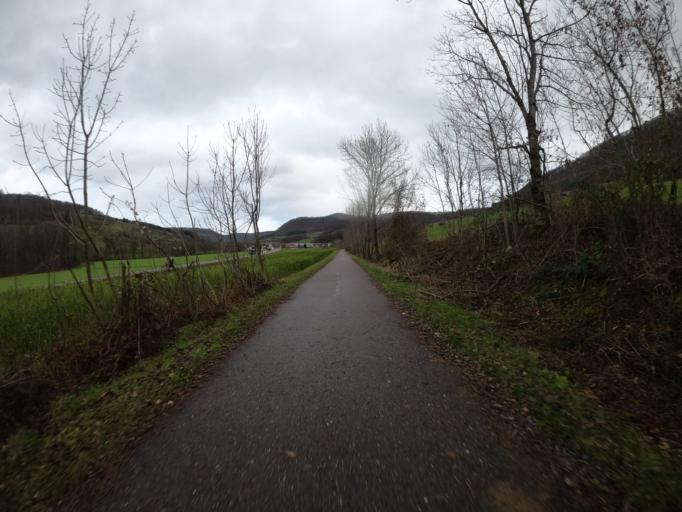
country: DE
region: Baden-Wuerttemberg
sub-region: Regierungsbezirk Stuttgart
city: Donzdorf
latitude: 48.6982
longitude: 9.8287
